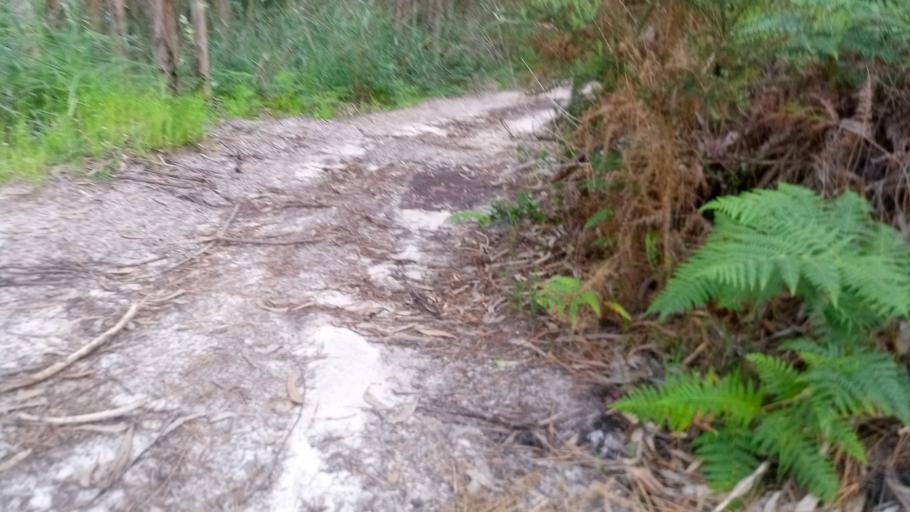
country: PT
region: Leiria
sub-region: Obidos
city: Obidos
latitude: 39.3932
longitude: -9.2087
